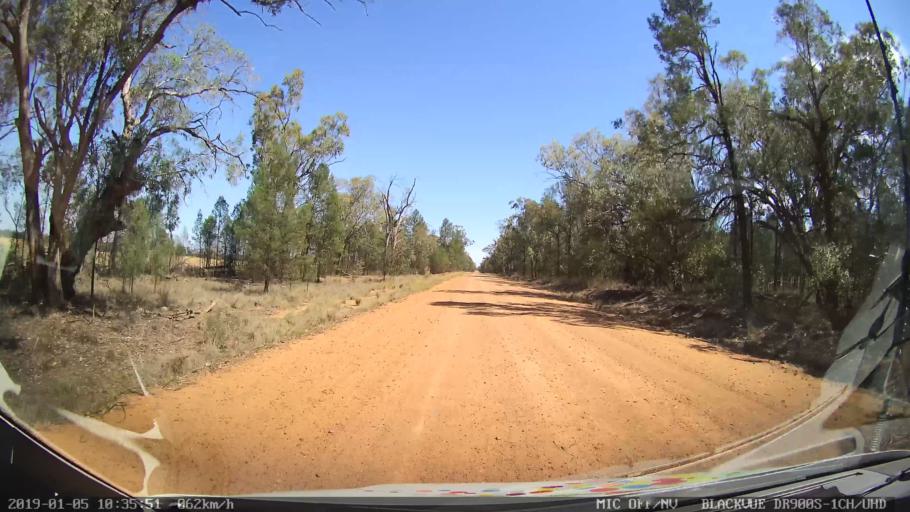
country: AU
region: New South Wales
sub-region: Gilgandra
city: Gilgandra
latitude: -31.4868
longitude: 148.9273
